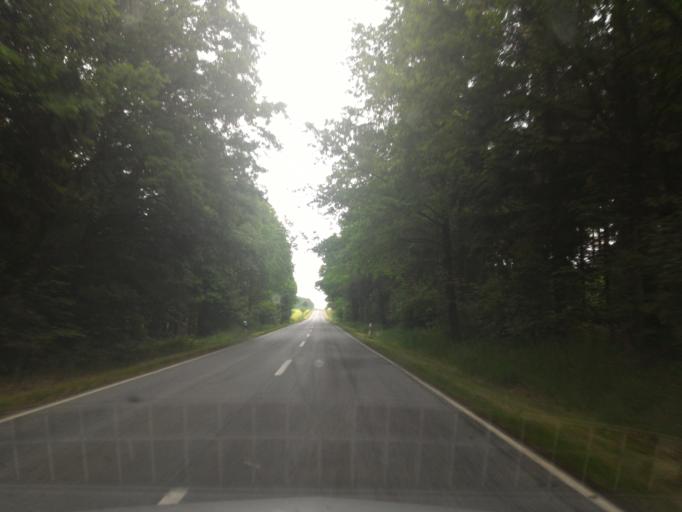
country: DE
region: Saxony
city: Leutersdorf
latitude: 50.9509
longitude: 14.6811
